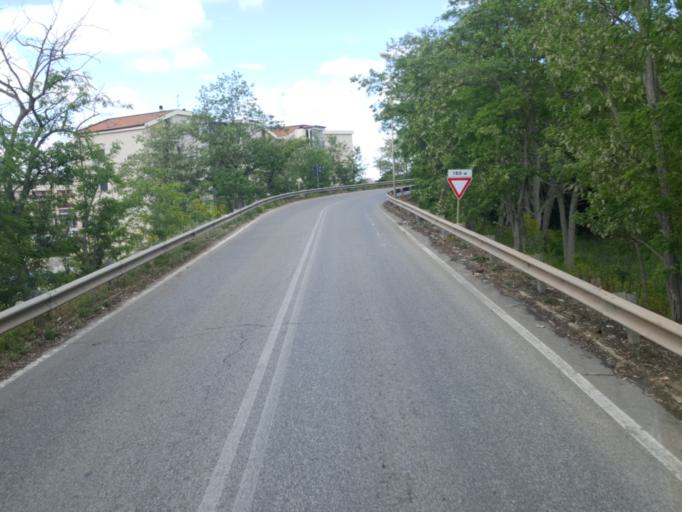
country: IT
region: Apulia
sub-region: Provincia di Bari
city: Altamura
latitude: 40.8142
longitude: 16.5533
